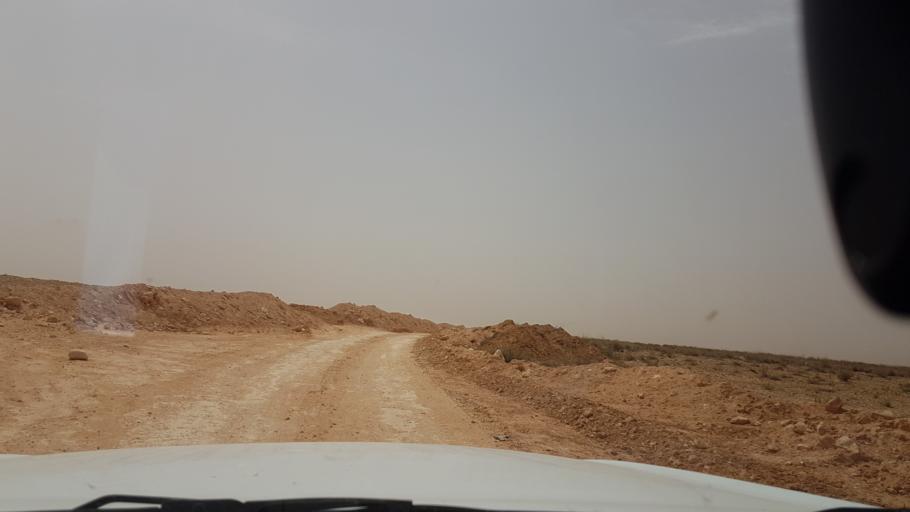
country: TN
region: Madanin
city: Medenine
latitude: 33.2811
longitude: 10.5947
